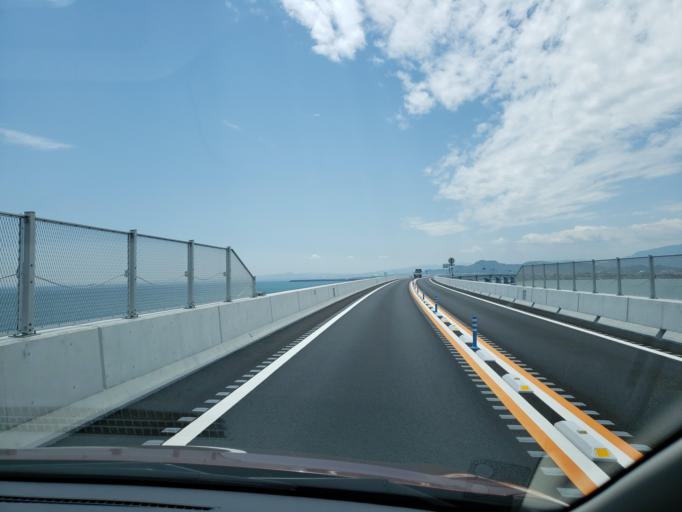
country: JP
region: Tokushima
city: Tokushima-shi
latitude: 34.0845
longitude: 134.6013
